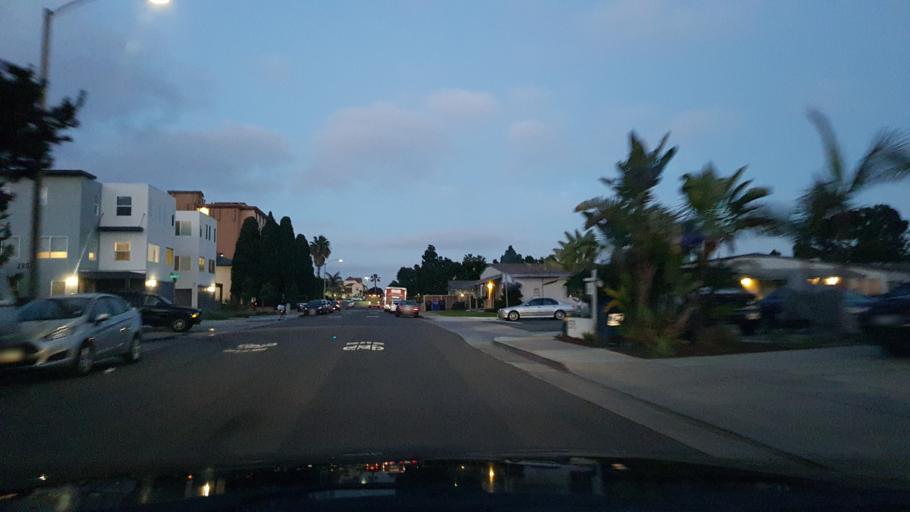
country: US
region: California
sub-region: San Diego County
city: Coronado
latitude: 32.7265
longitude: -117.2261
